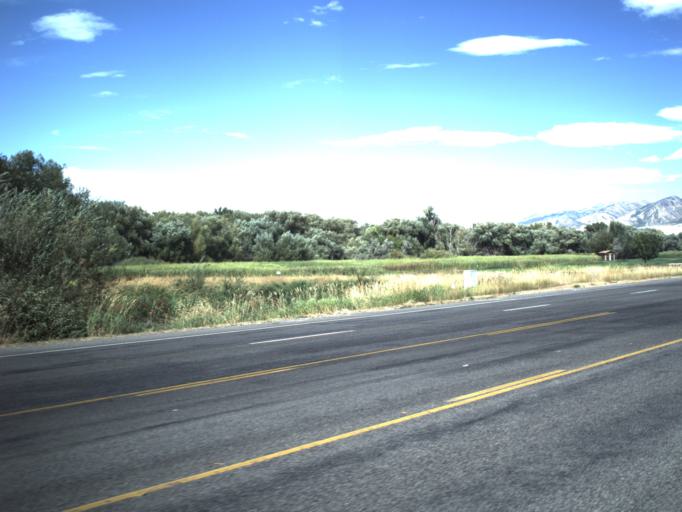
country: US
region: Utah
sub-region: Cache County
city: River Heights
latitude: 41.7071
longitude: -111.8464
